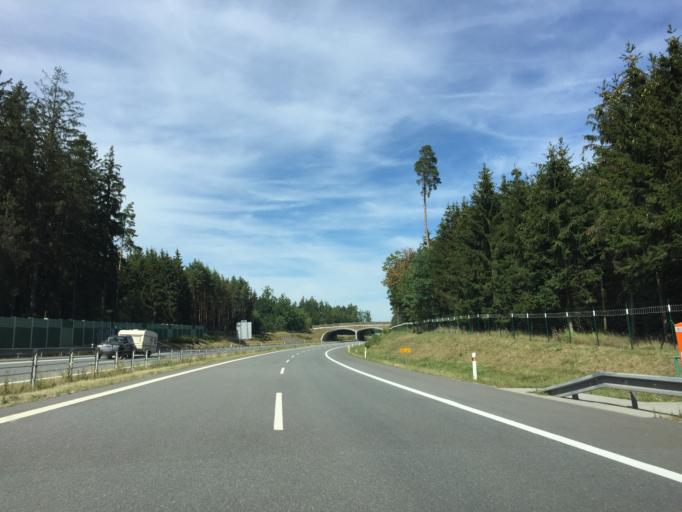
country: CZ
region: Jihocesky
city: Plana nad Luznici
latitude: 49.3742
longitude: 14.7205
